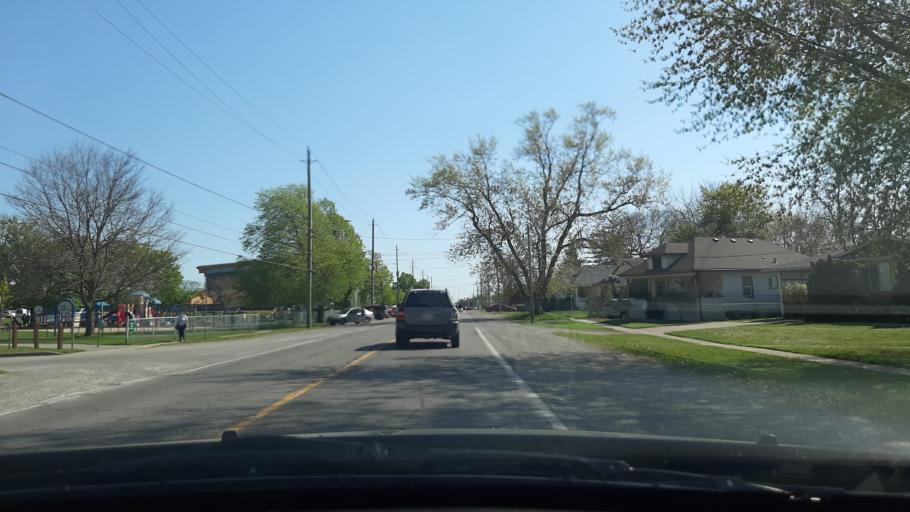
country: CA
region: Ontario
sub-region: Regional Municipality of Niagara
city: St. Catharines
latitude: 43.1829
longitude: -79.2259
